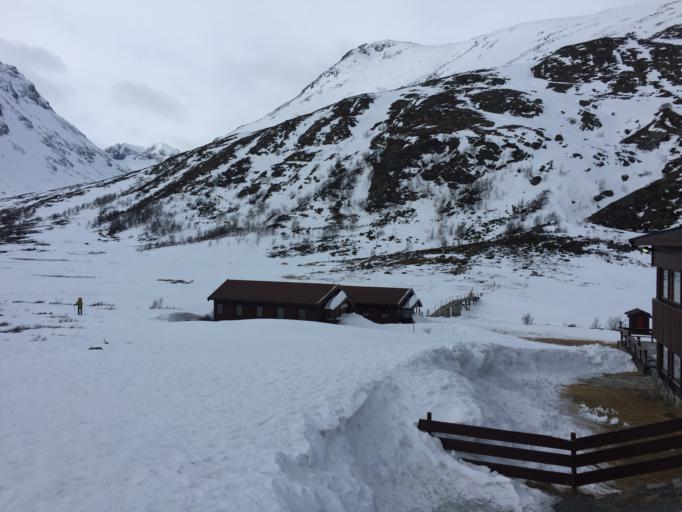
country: NO
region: Oppland
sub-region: Lom
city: Fossbergom
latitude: 61.6246
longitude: 8.4049
